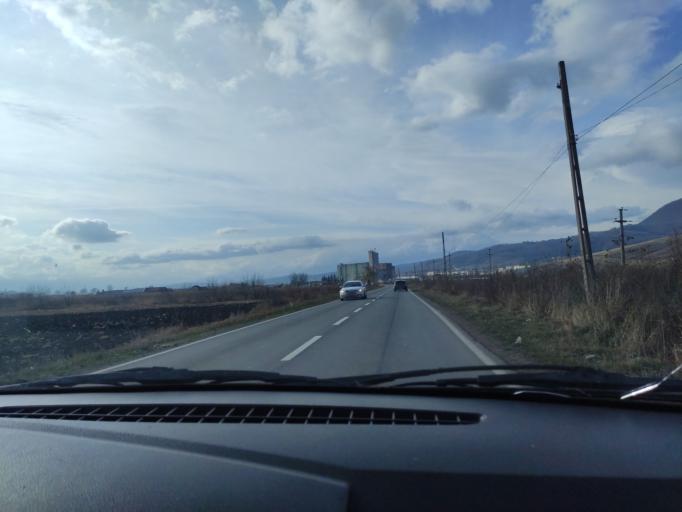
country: RO
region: Brasov
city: Codlea
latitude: 45.7134
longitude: 25.4664
